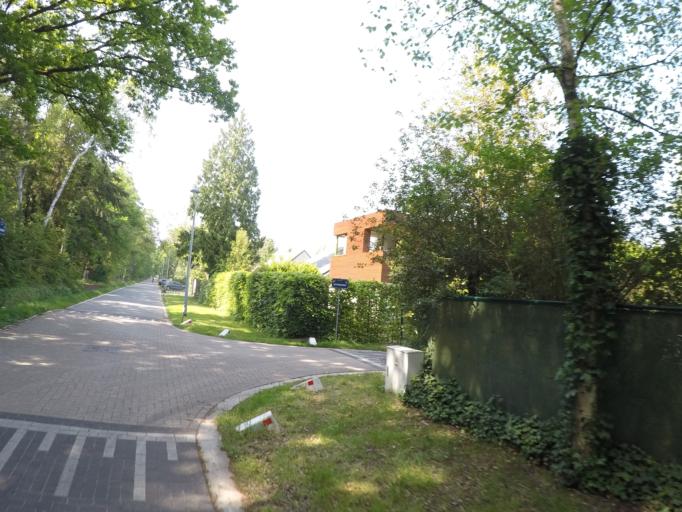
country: BE
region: Flanders
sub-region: Provincie Antwerpen
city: Schilde
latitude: 51.2898
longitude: 4.5507
